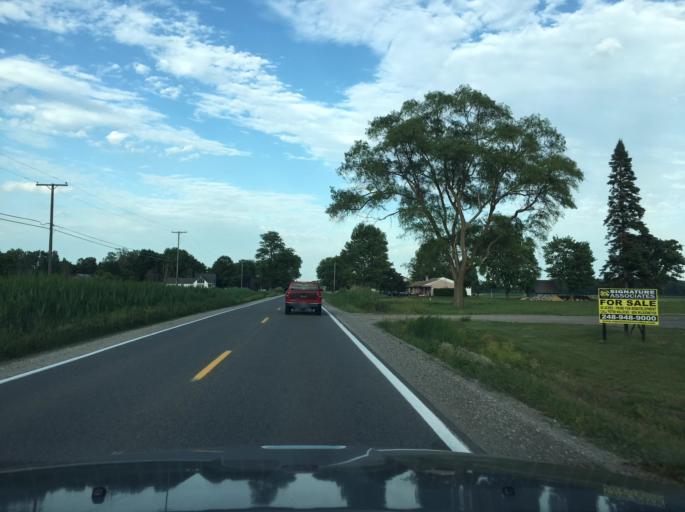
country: US
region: Michigan
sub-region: Macomb County
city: Shelby
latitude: 42.7168
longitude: -82.9270
